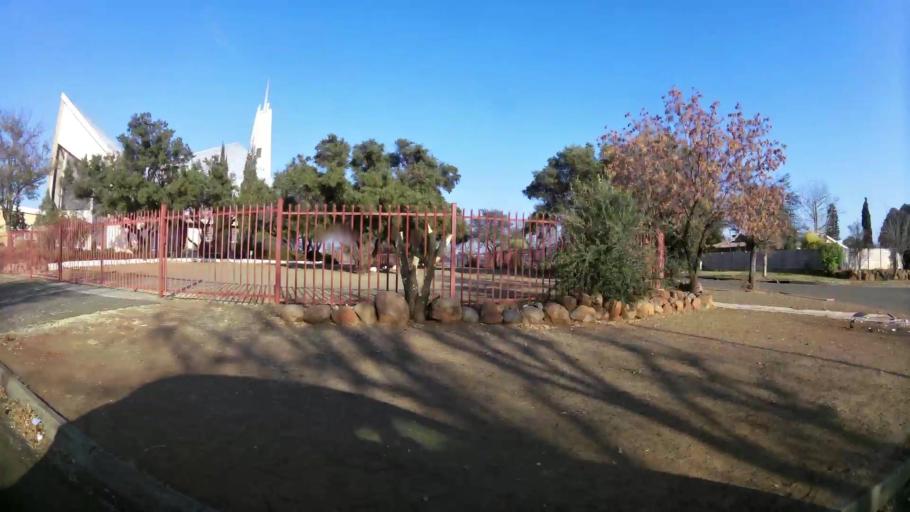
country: ZA
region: Orange Free State
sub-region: Mangaung Metropolitan Municipality
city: Bloemfontein
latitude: -29.1447
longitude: 26.2015
